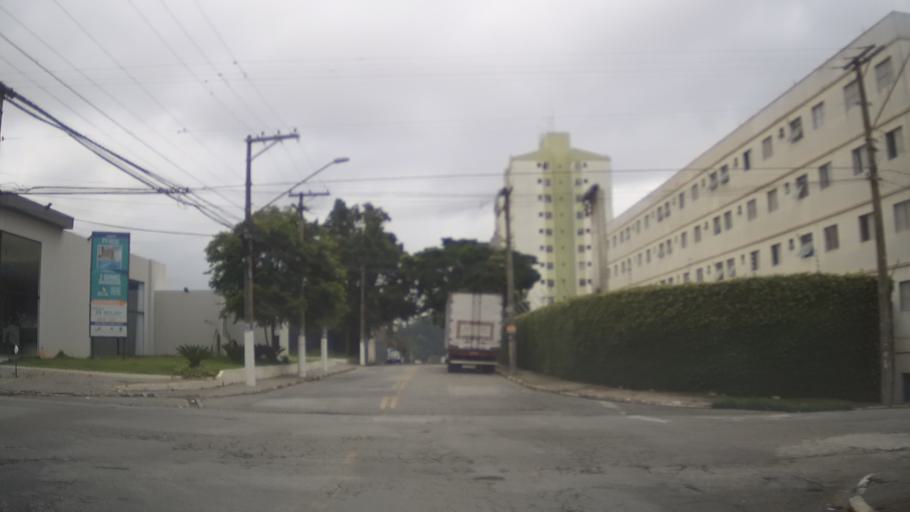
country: BR
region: Sao Paulo
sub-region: Guarulhos
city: Guarulhos
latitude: -23.4829
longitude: -46.5505
